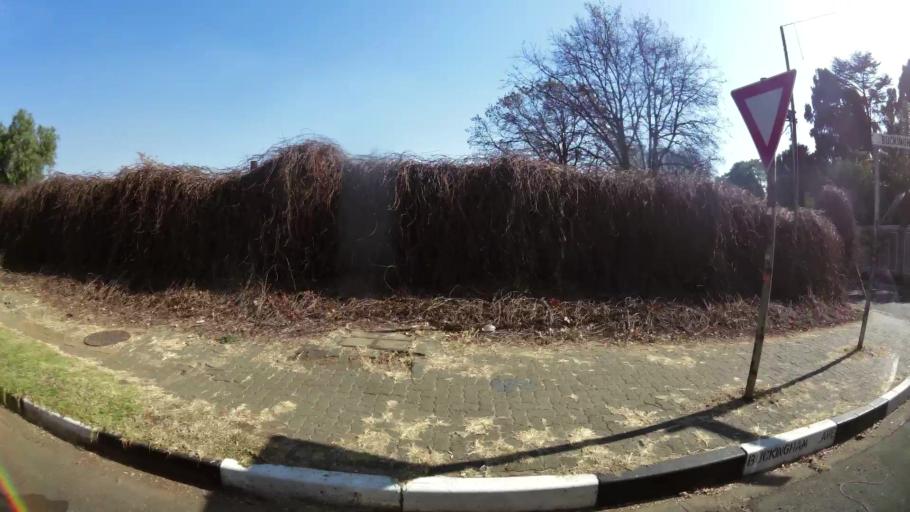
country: ZA
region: Gauteng
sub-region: City of Johannesburg Metropolitan Municipality
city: Johannesburg
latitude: -26.1324
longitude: 28.0294
